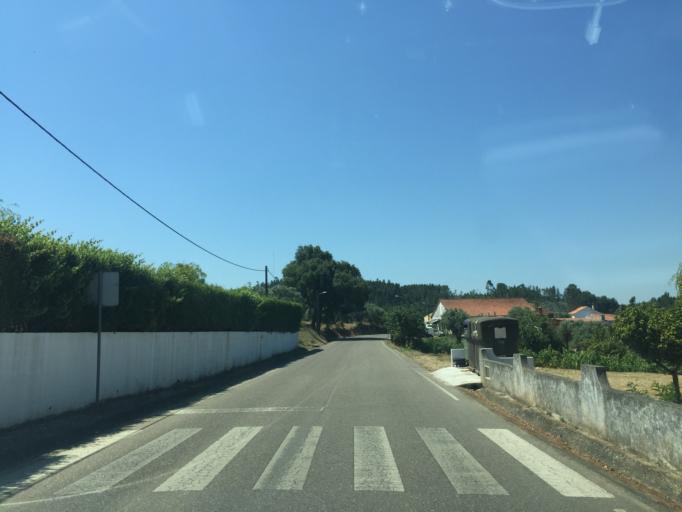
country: PT
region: Santarem
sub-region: Ferreira do Zezere
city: Ferreira do Zezere
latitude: 39.6192
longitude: -8.3114
